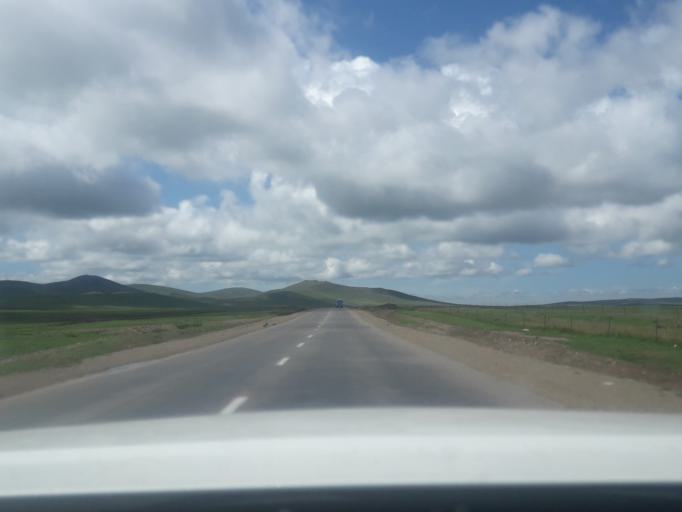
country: MN
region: Central Aimak
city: Altanbulag
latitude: 47.9004
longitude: 106.4568
